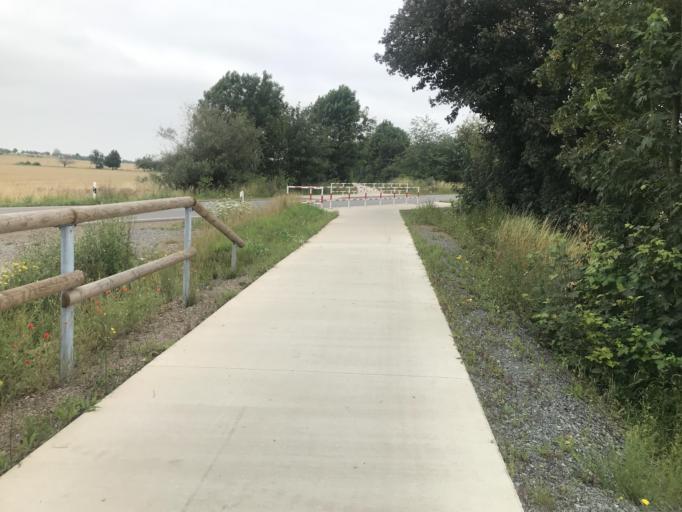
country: DE
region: Saxony-Anhalt
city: Ballenstedt
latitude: 51.7242
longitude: 11.2095
